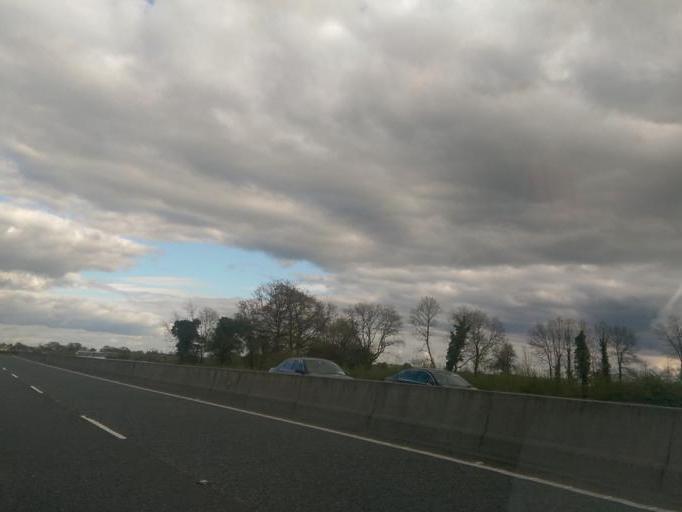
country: IE
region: Leinster
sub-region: Uibh Fhaili
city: Clara
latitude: 53.3933
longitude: -7.6239
